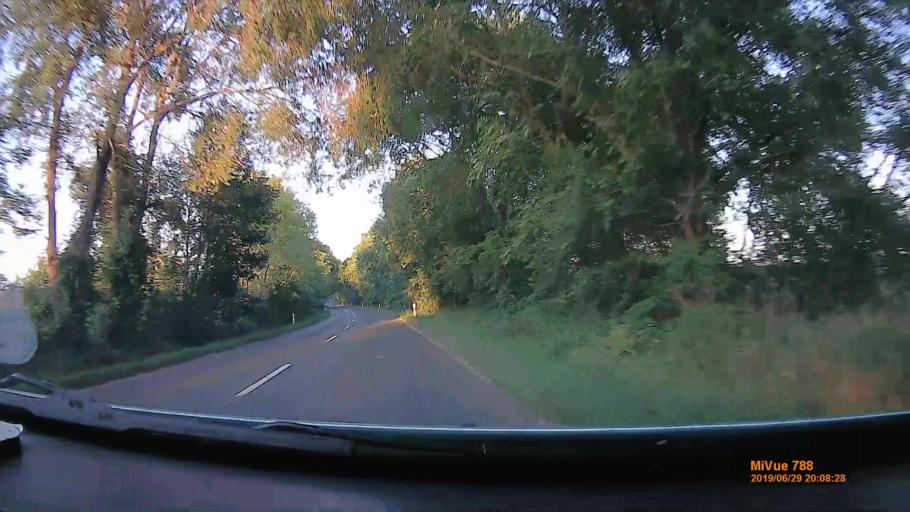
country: HU
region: Pest
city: Zsambek
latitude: 47.5421
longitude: 18.7418
